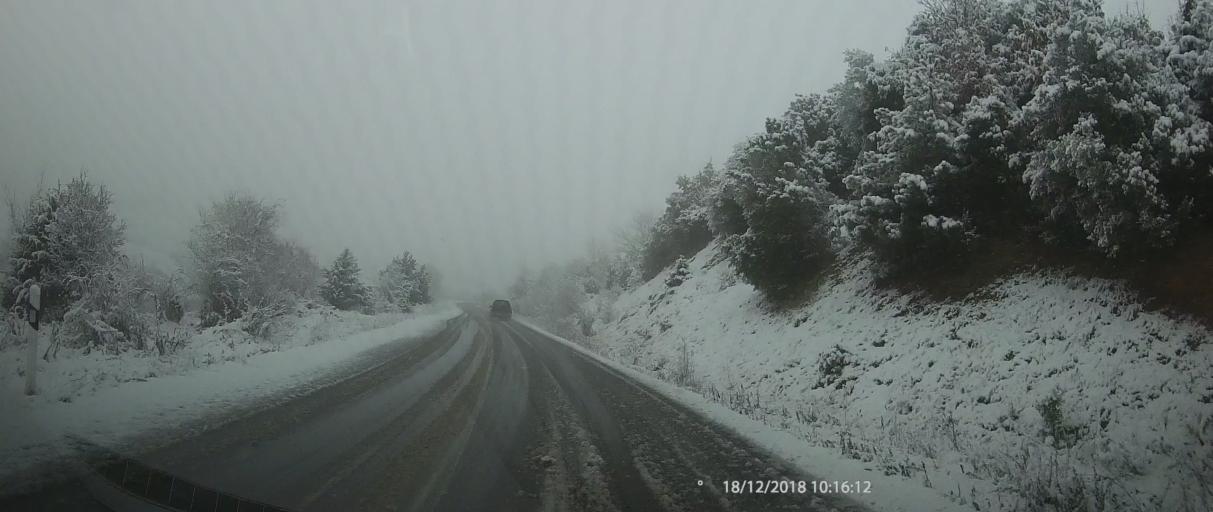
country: GR
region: Thessaly
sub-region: Nomos Larisis
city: Livadi
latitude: 40.1142
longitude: 22.2103
